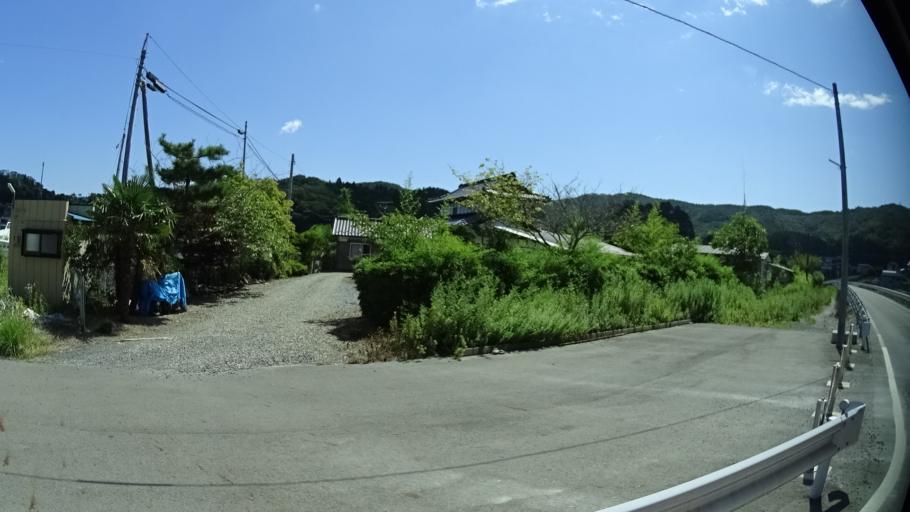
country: JP
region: Iwate
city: Ofunato
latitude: 39.0151
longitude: 141.7140
